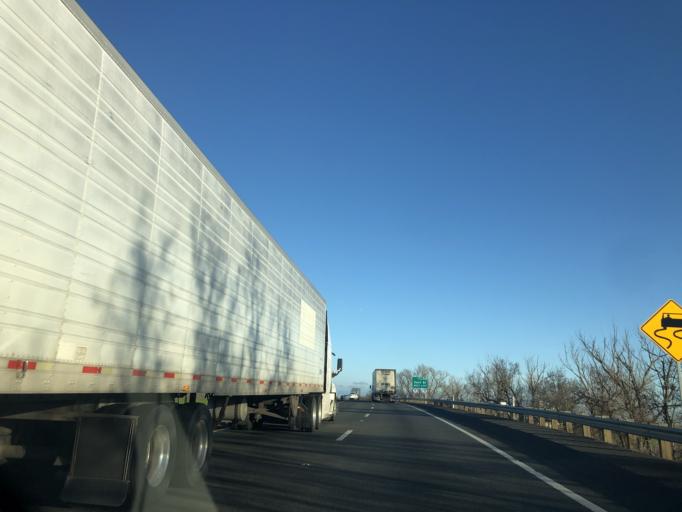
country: US
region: California
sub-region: Yolo County
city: Woodland
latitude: 38.6995
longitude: -121.7794
